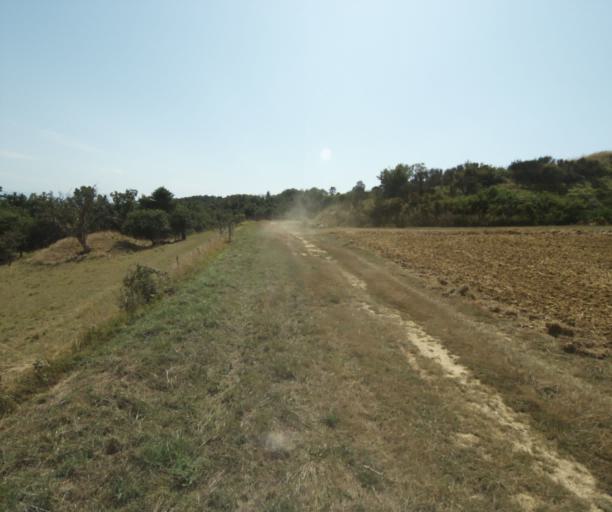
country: FR
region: Midi-Pyrenees
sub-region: Departement de la Haute-Garonne
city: Saint-Felix-Lauragais
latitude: 43.4417
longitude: 1.8766
